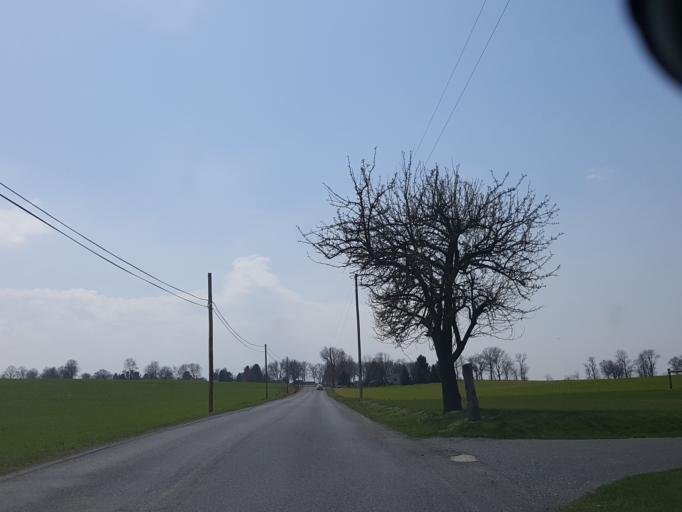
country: US
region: Pennsylvania
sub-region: Lebanon County
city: Annville
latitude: 40.3114
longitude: -76.5263
